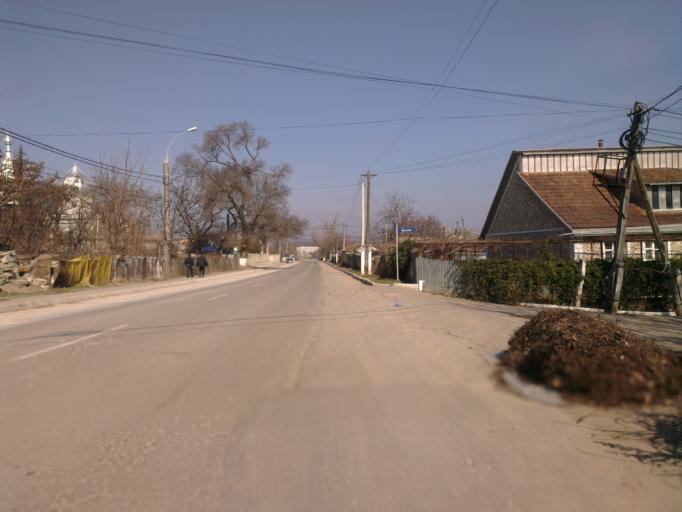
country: MD
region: Chisinau
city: Cricova
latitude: 47.1343
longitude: 28.8666
